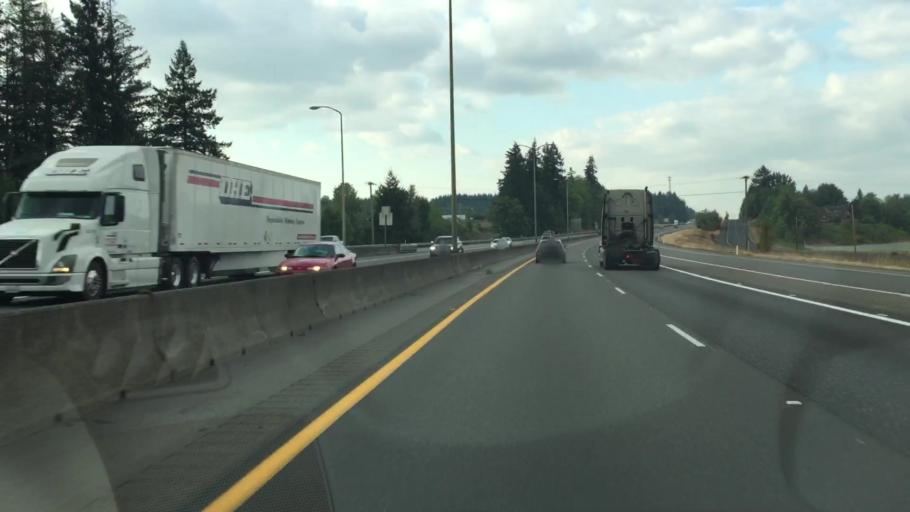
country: US
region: Washington
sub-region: Lewis County
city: Winlock
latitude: 46.4193
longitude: -122.8906
